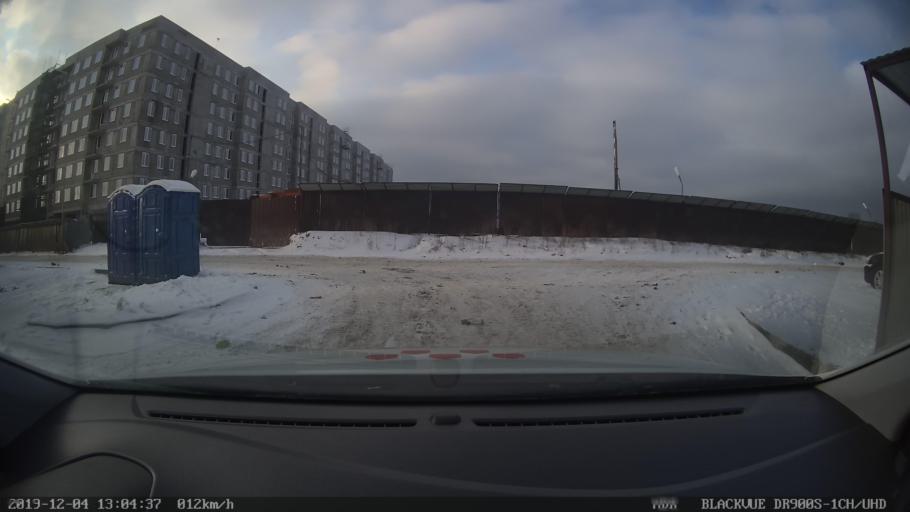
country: RU
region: Tatarstan
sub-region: Gorod Kazan'
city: Kazan
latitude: 55.8513
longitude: 49.0643
